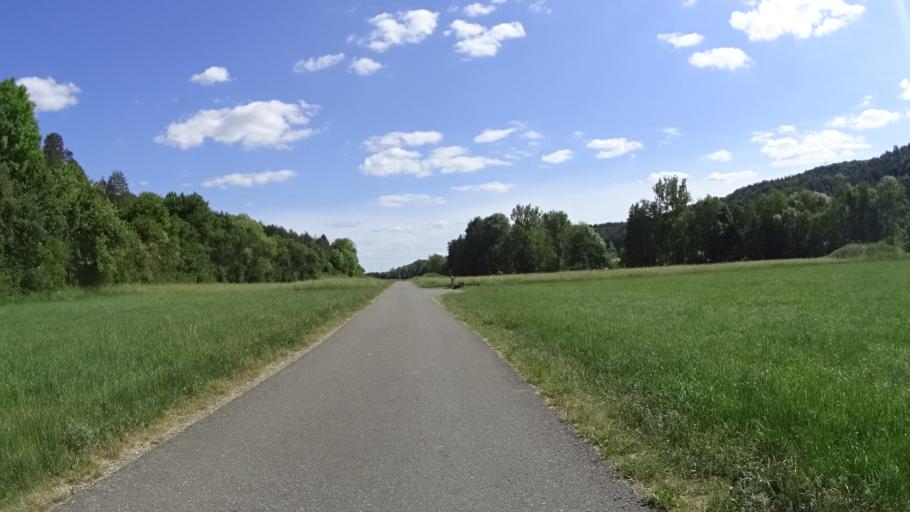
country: DE
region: Baden-Wuerttemberg
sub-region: Karlsruhe Region
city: Hardheim
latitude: 49.5973
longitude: 9.4789
